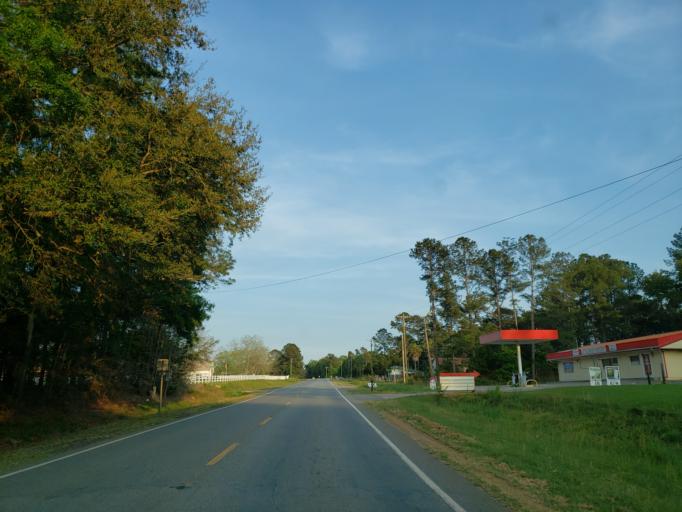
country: US
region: Georgia
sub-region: Lowndes County
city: Hahira
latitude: 30.9967
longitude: -83.4391
